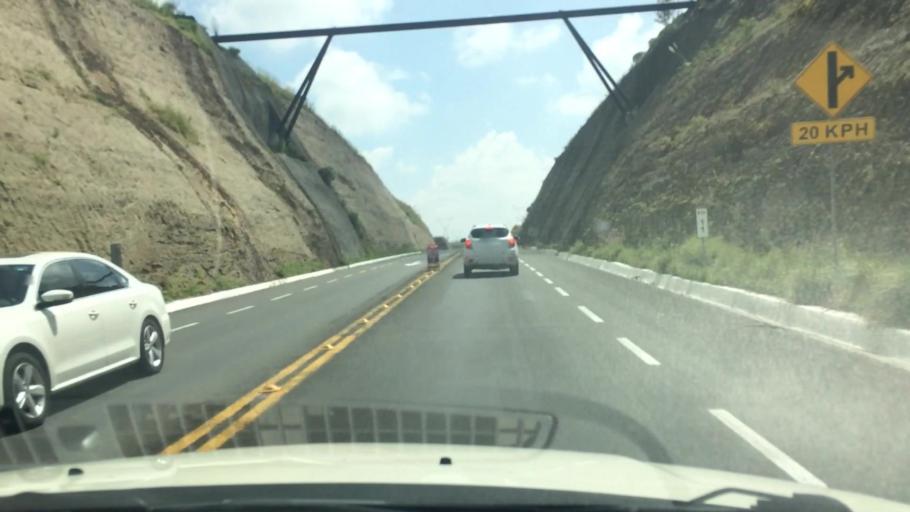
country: MX
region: Mexico
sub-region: Almoloya de Juarez
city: San Pedro de la Hortaliza (Ejido Almoloyan)
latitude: 19.3806
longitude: -99.8128
